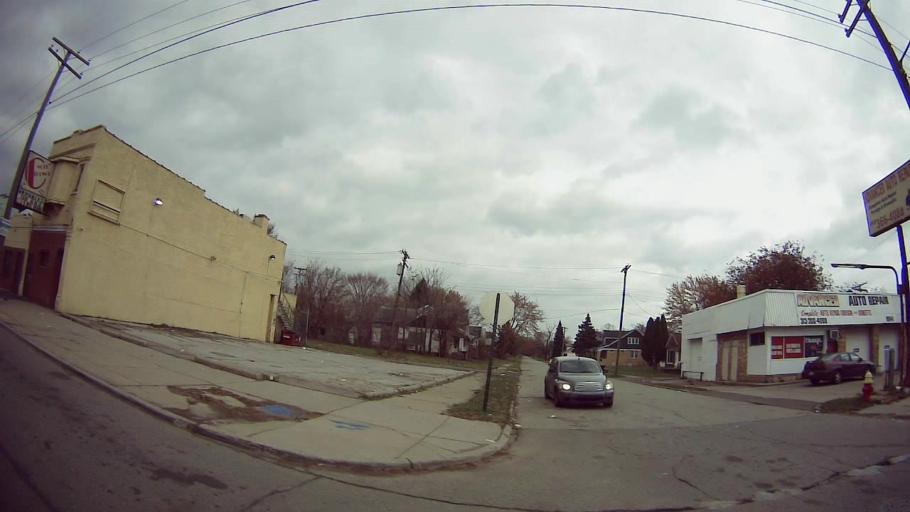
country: US
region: Michigan
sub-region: Macomb County
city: Warren
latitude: 42.4325
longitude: -83.0241
